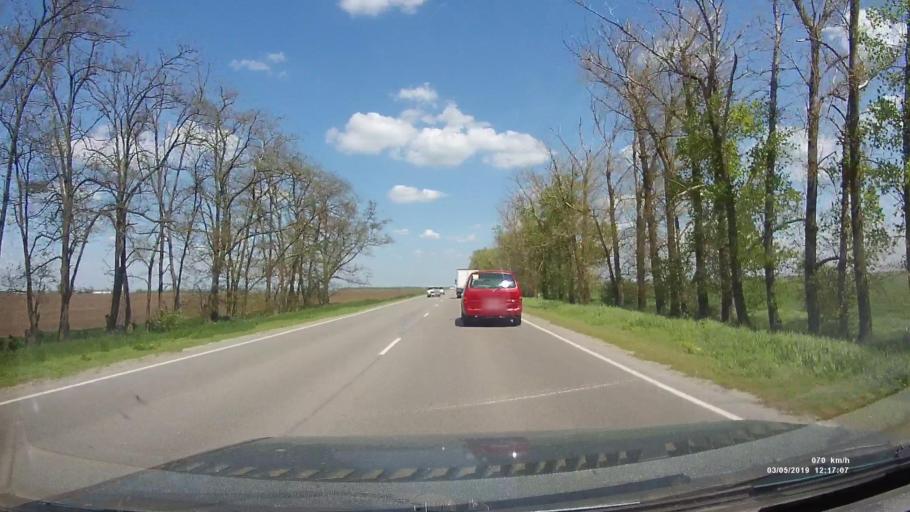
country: RU
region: Rostov
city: Melikhovskaya
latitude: 47.3795
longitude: 40.5899
